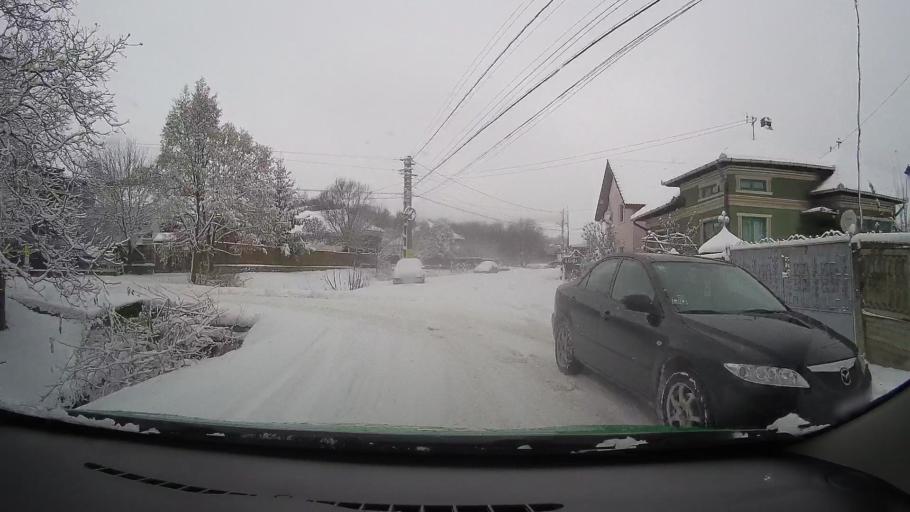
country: RO
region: Hunedoara
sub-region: Comuna Carjiti
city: Carjiti
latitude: 45.8470
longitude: 22.8627
